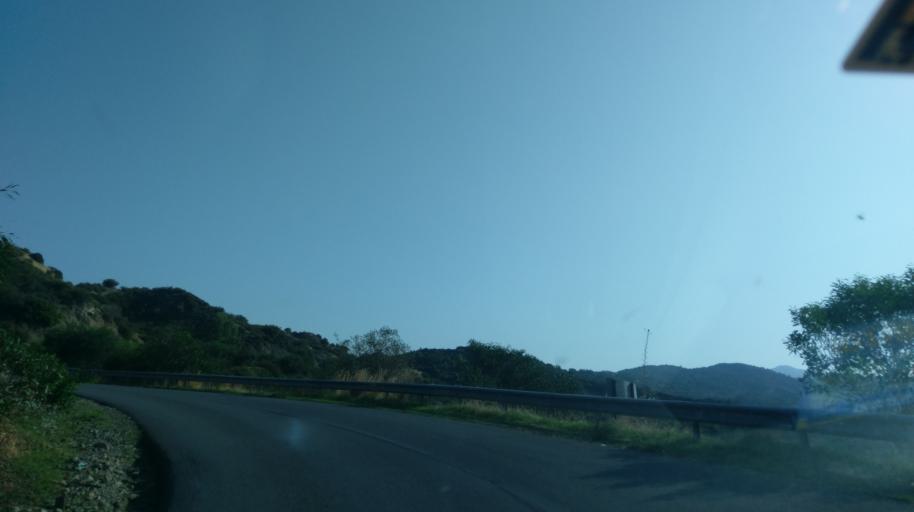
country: CY
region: Lefkosia
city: Kato Pyrgos
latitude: 35.1635
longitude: 32.7530
